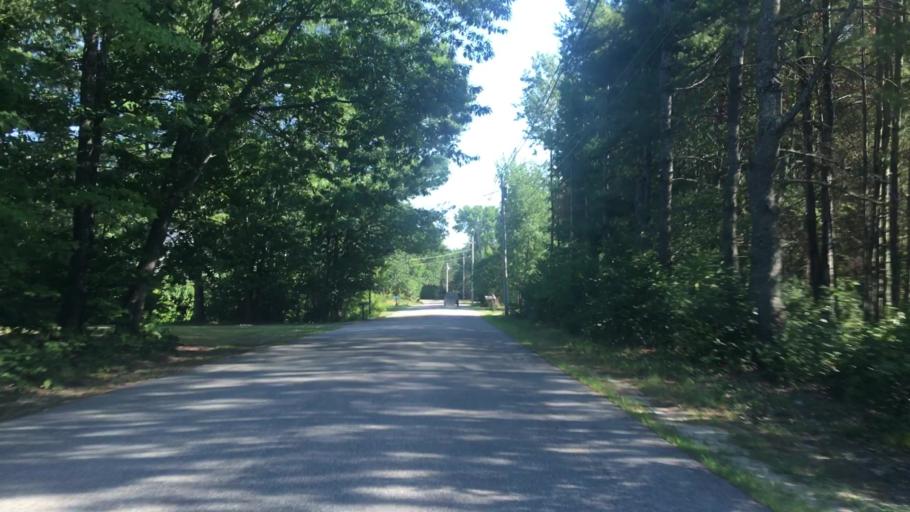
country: US
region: Maine
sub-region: Cumberland County
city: Gorham
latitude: 43.7266
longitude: -70.5162
